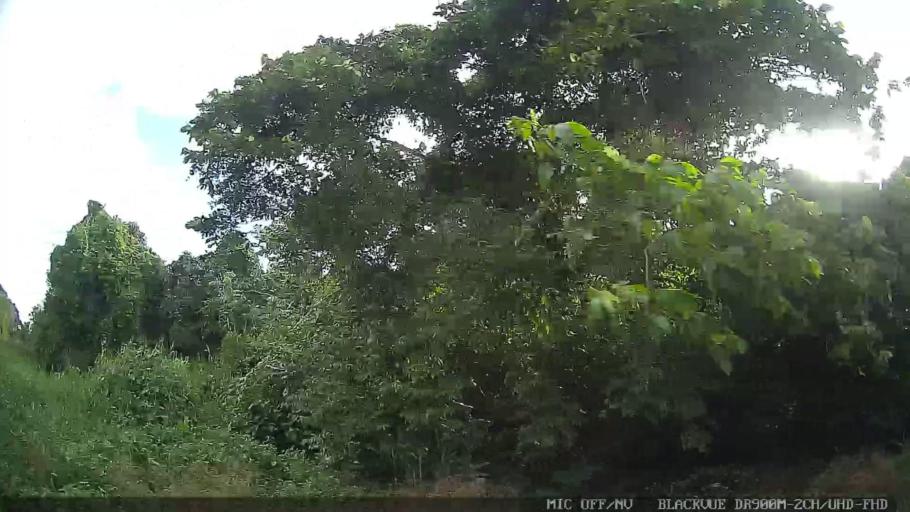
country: BR
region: Sao Paulo
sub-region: Itanhaem
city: Itanhaem
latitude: -24.1949
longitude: -46.8249
